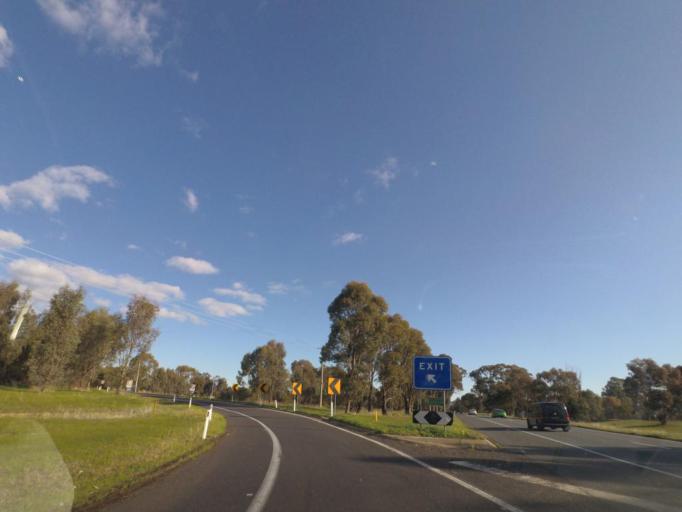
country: AU
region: Victoria
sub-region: Benalla
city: Benalla
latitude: -36.6941
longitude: 145.6594
